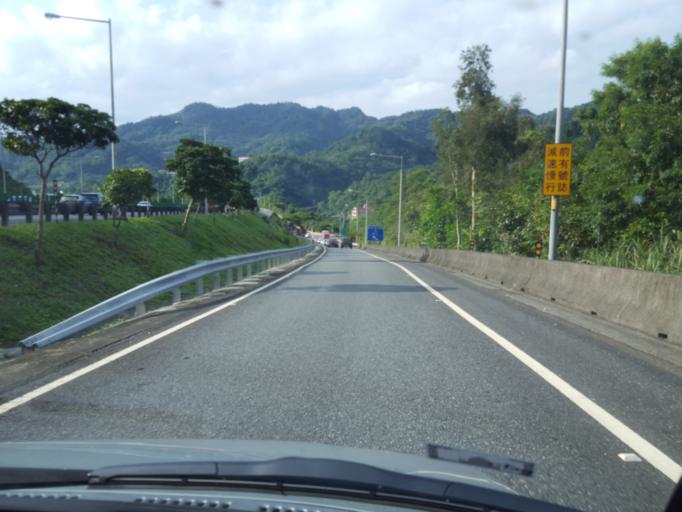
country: TW
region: Taipei
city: Taipei
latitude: 25.0064
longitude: 121.6496
